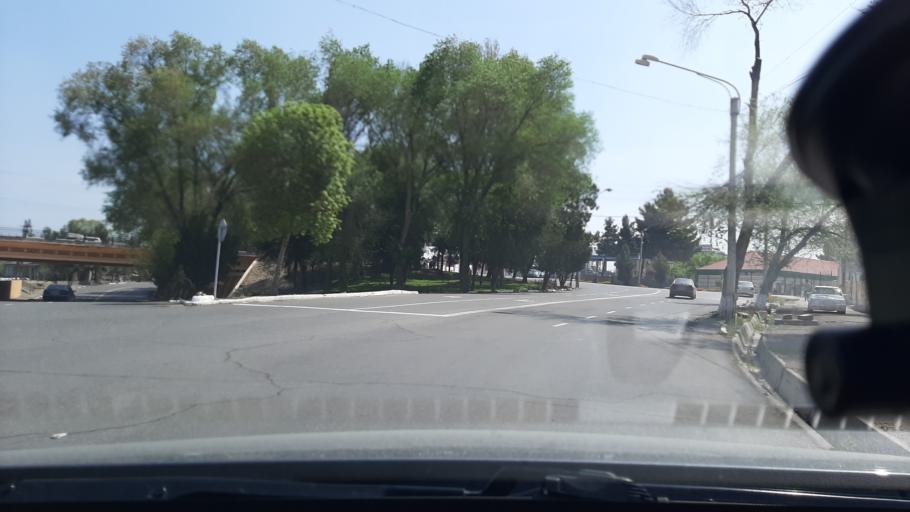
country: TJ
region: Viloyati Sughd
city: Khujand
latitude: 40.2928
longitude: 69.6389
